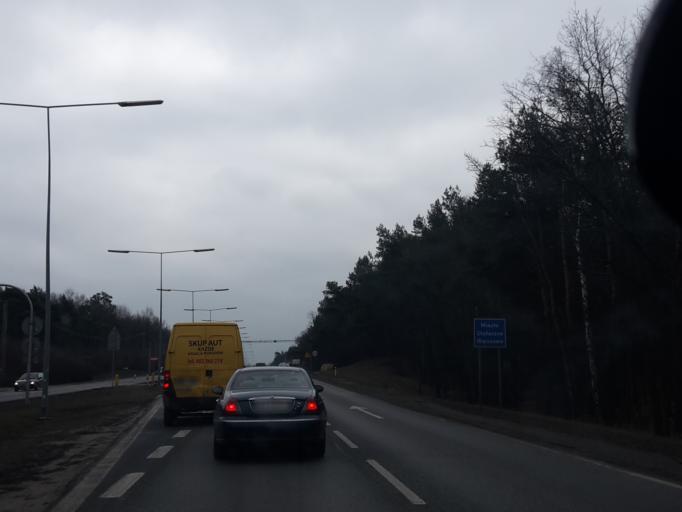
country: PL
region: Masovian Voivodeship
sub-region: Powiat warszawski zachodni
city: Lomianki
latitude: 52.3223
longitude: 20.9121
